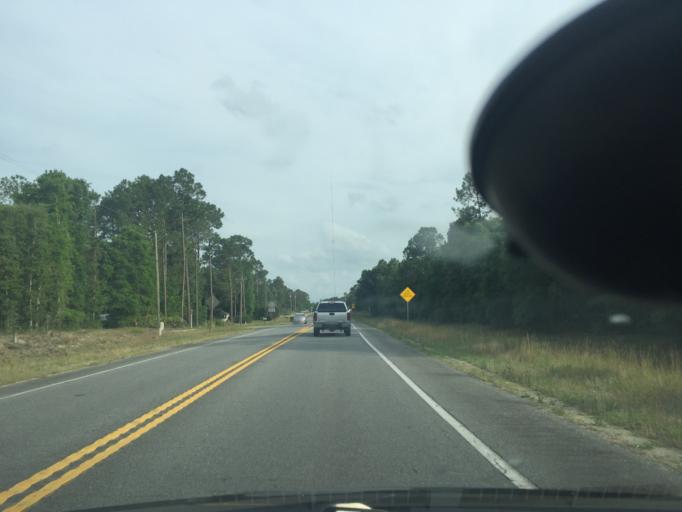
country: US
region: Georgia
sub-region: Chatham County
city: Bloomingdale
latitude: 32.0694
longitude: -81.3590
